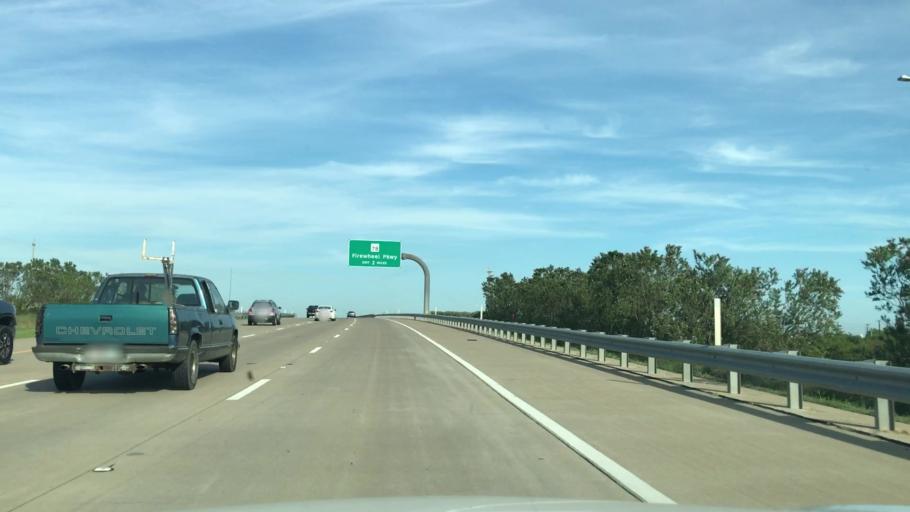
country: US
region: Texas
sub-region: Dallas County
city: Sachse
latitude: 32.9502
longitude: -96.5680
